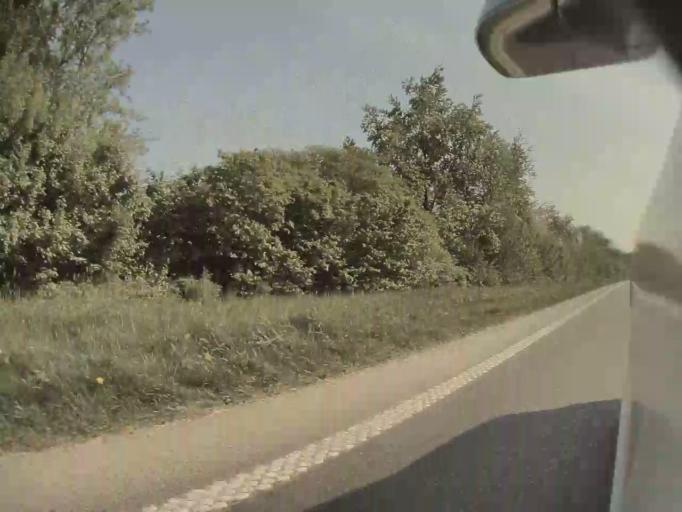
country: BE
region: Wallonia
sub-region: Province de Namur
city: Ciney
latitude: 50.3029
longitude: 5.1212
